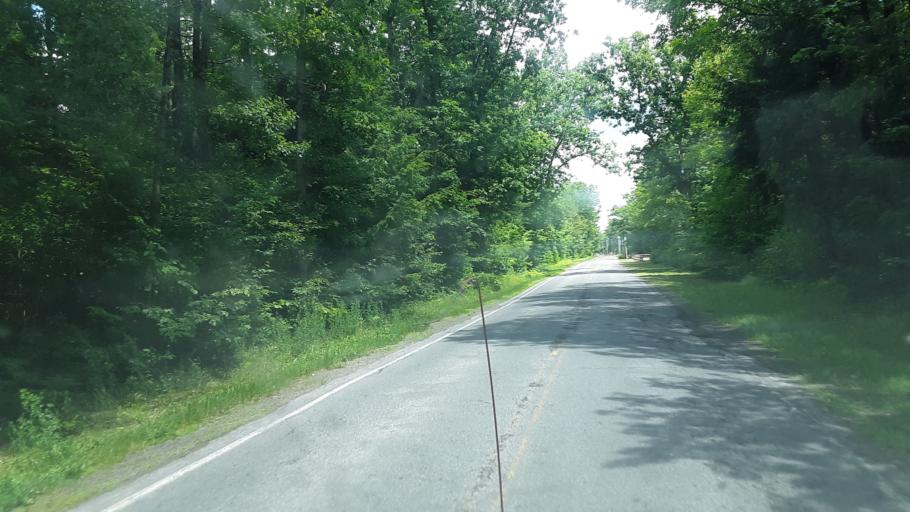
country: US
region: New York
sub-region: Oneida County
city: Rome
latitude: 43.2630
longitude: -75.5754
